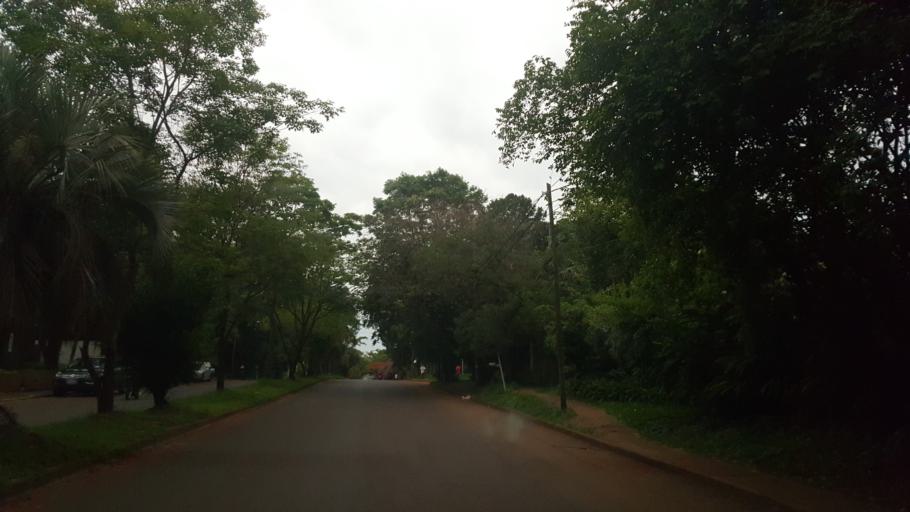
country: AR
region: Misiones
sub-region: Departamento de Capital
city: Posadas
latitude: -27.3607
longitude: -55.9308
